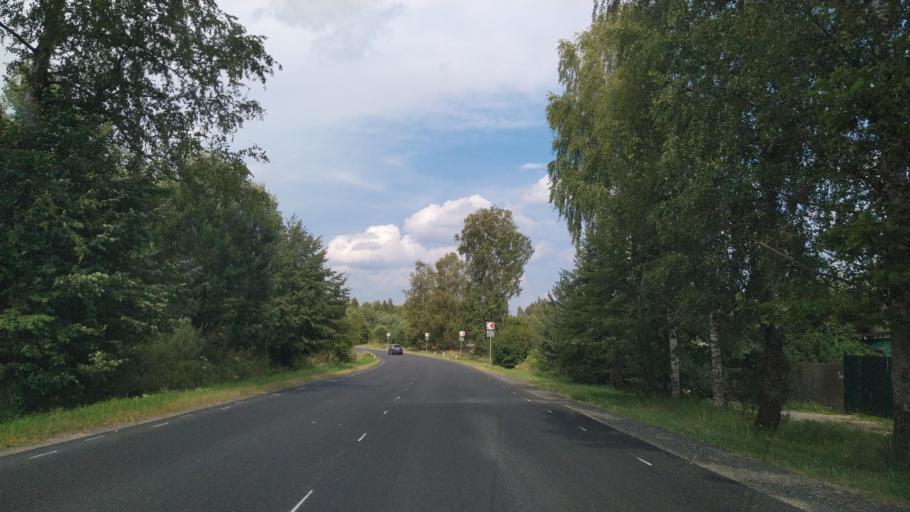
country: RU
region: Pskov
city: Porkhov
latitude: 57.8317
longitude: 29.5337
